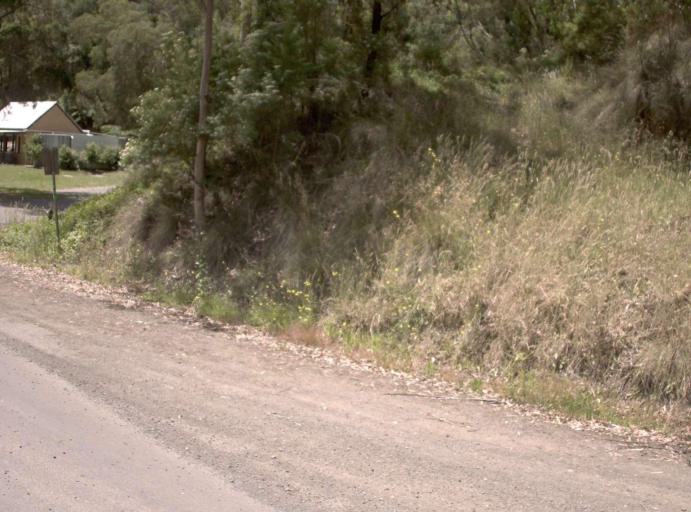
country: AU
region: Victoria
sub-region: Latrobe
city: Traralgon
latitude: -37.9497
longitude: 146.4499
